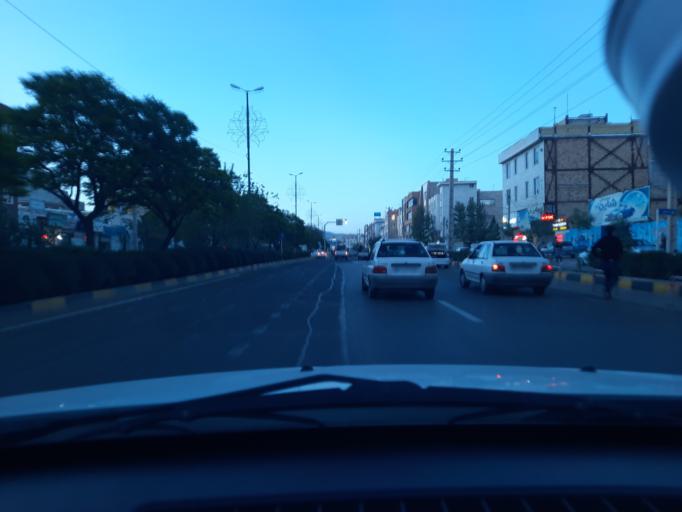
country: IR
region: Qazvin
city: Qazvin
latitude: 36.3097
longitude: 50.0132
